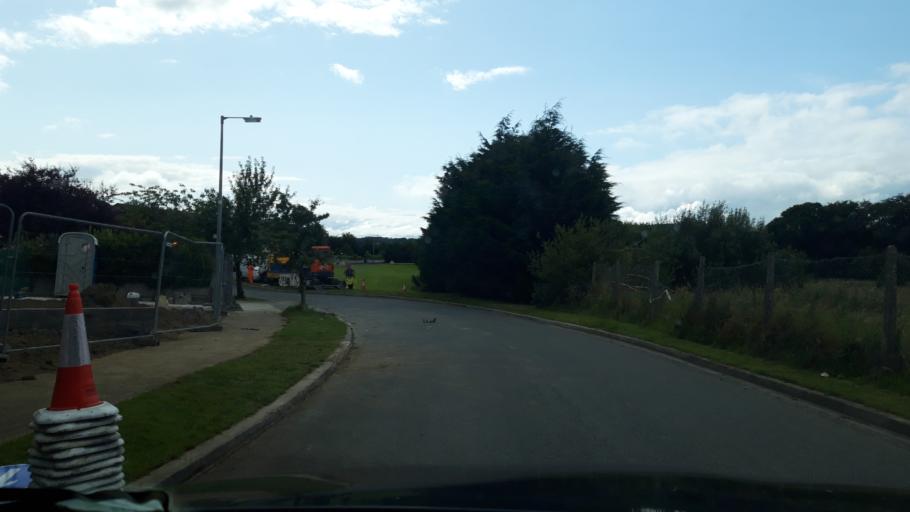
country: IE
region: Leinster
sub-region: Wicklow
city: Blessington
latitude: 53.1760
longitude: -6.5317
